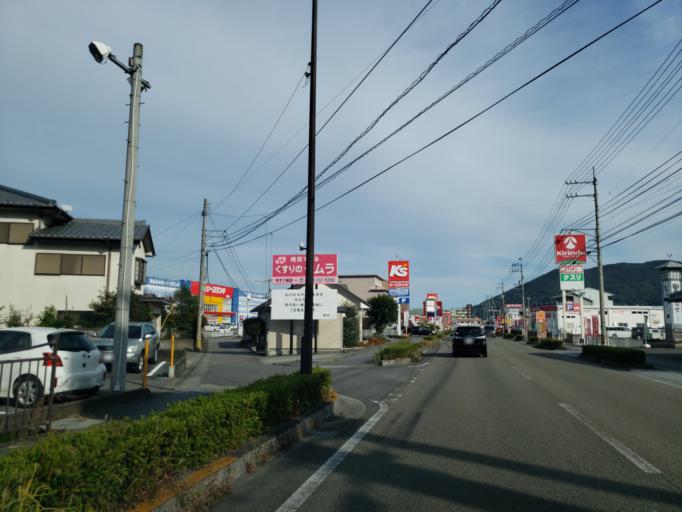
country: JP
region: Tokushima
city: Wakimachi
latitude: 34.0642
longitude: 134.1581
